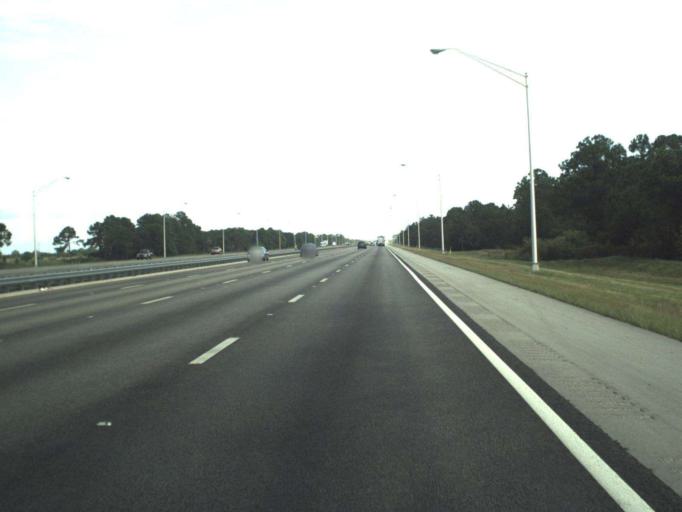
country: US
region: Florida
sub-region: Saint Lucie County
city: Lakewood Park
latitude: 27.4836
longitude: -80.4344
